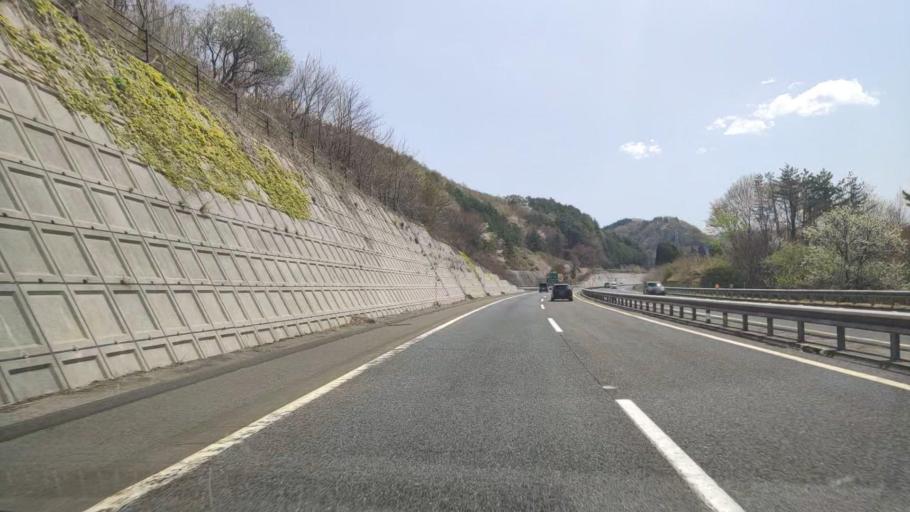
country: JP
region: Iwate
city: Ichinohe
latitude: 40.2293
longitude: 141.3195
